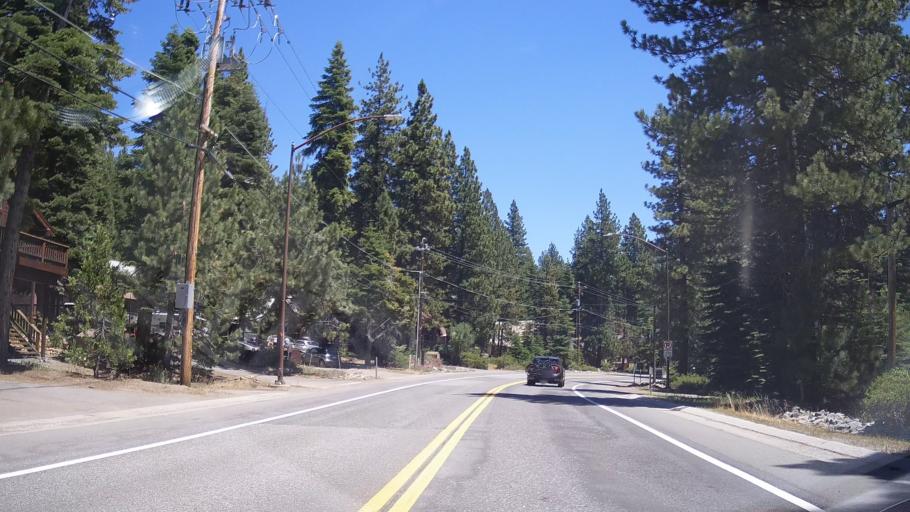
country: US
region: California
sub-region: Placer County
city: Dollar Point
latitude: 39.2081
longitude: -120.0928
